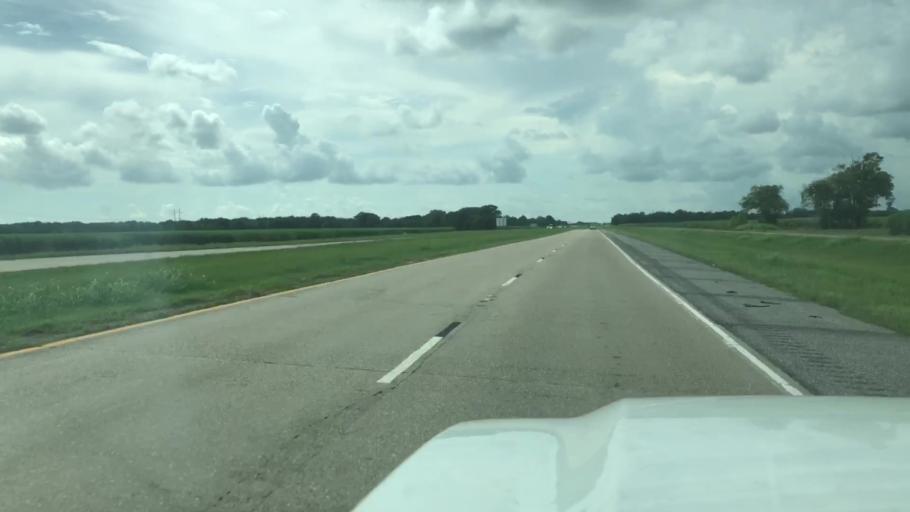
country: US
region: Louisiana
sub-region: Saint Mary Parish
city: Franklin
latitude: 29.7586
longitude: -91.4743
